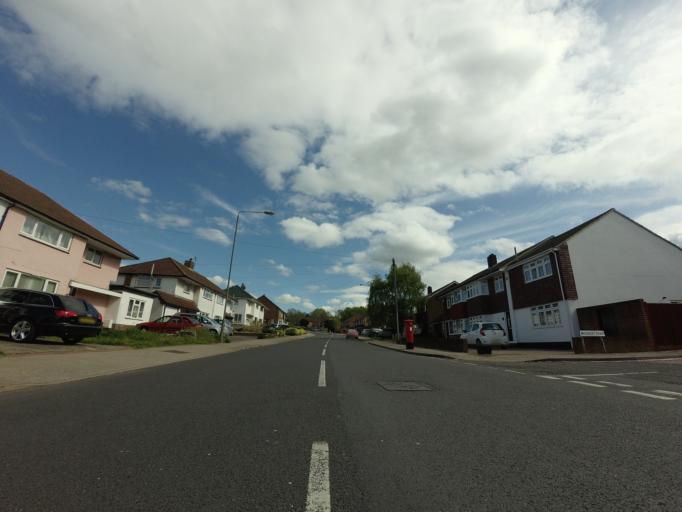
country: GB
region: England
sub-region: Greater London
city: Orpington
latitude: 51.3710
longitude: 0.1138
